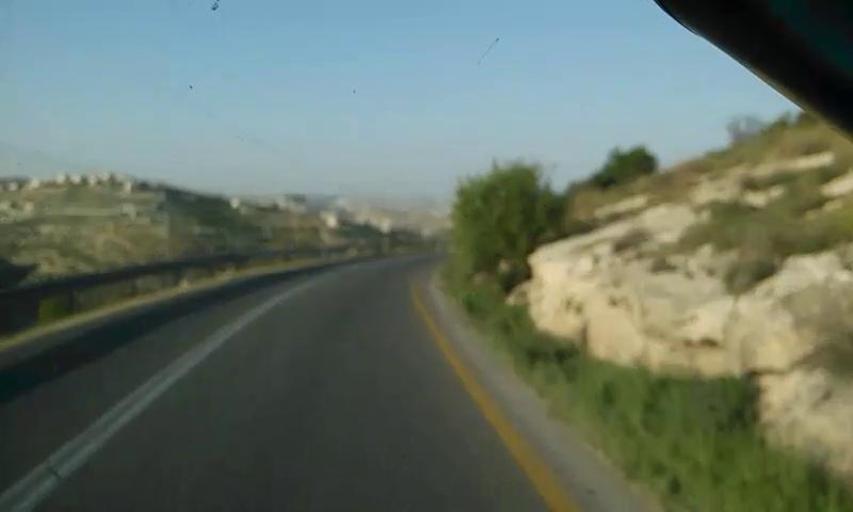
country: PS
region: West Bank
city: Marah Rabbah
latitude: 31.6496
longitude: 35.2043
